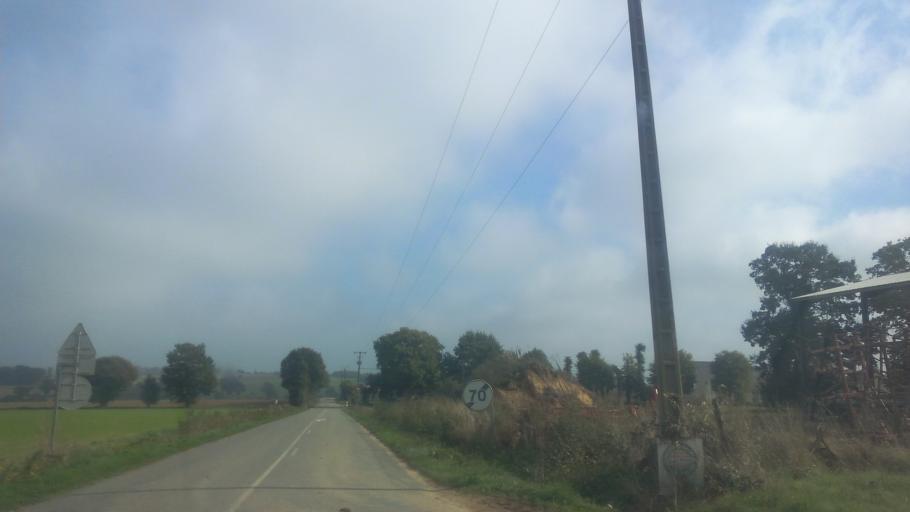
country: FR
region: Pays de la Loire
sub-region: Departement de la Loire-Atlantique
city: Conquereuil
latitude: 47.6262
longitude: -1.7792
